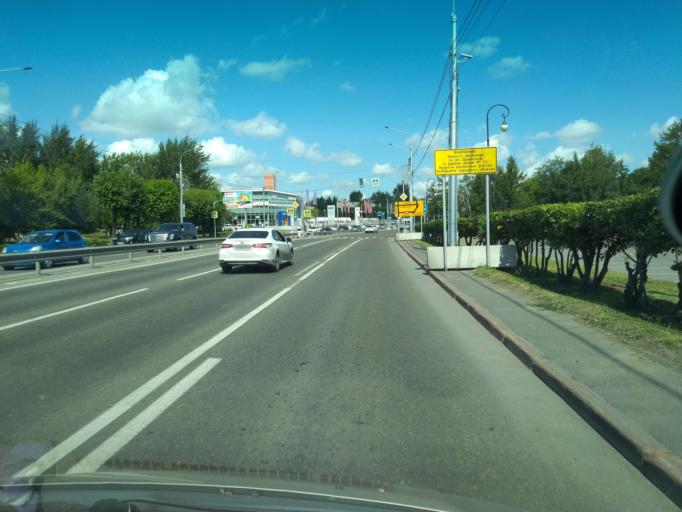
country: RU
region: Krasnoyarskiy
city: Krasnoyarsk
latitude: 56.0228
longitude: 92.8853
